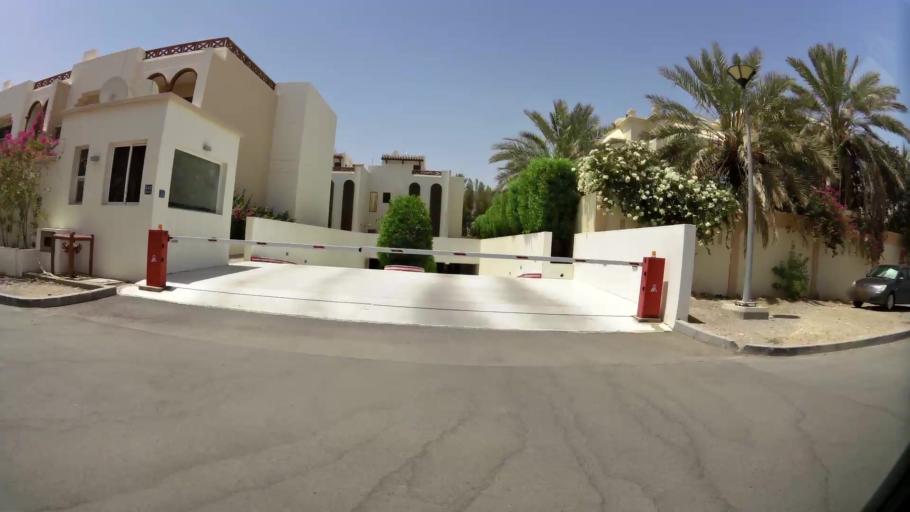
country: OM
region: Muhafazat Masqat
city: Bawshar
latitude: 23.6009
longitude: 58.4745
